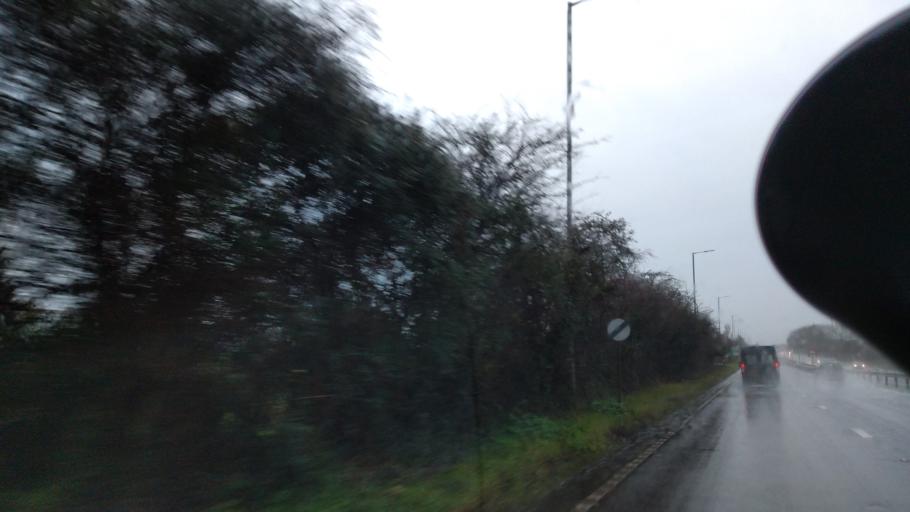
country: GB
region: England
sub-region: West Sussex
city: Broadwater
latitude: 50.8360
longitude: -0.3572
